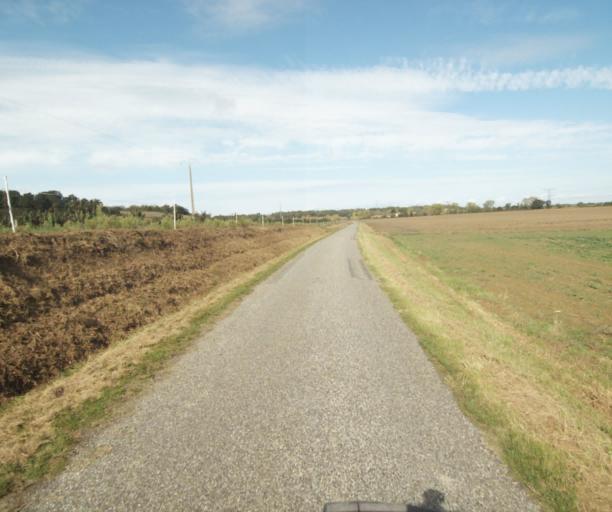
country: FR
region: Midi-Pyrenees
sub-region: Departement du Tarn-et-Garonne
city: Verdun-sur-Garonne
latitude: 43.8492
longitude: 1.1962
